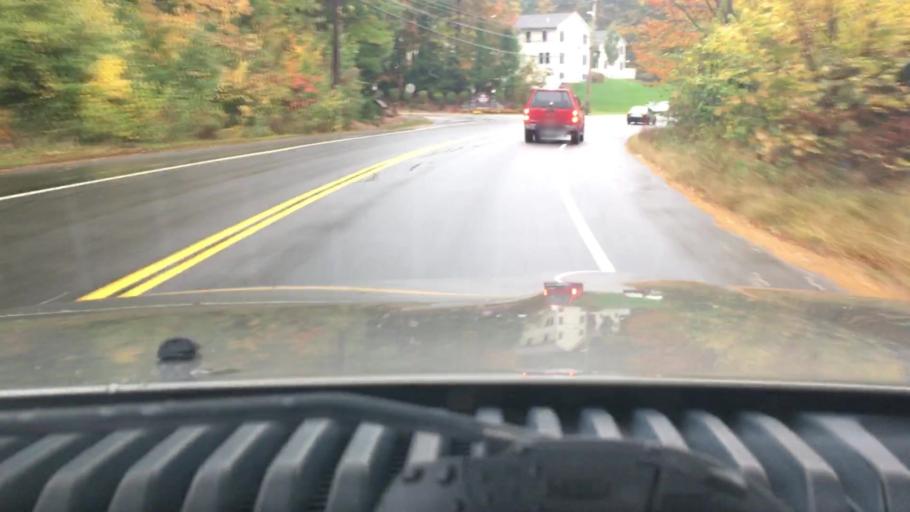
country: US
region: New Hampshire
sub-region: Hillsborough County
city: Pinardville
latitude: 43.0288
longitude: -71.4846
